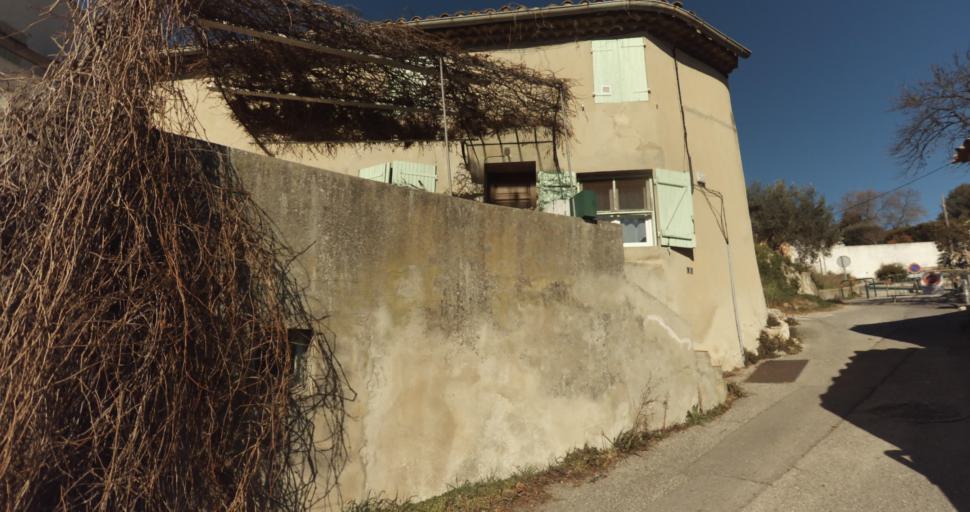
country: FR
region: Provence-Alpes-Cote d'Azur
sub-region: Departement des Bouches-du-Rhone
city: Peypin
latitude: 43.3867
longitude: 5.5794
